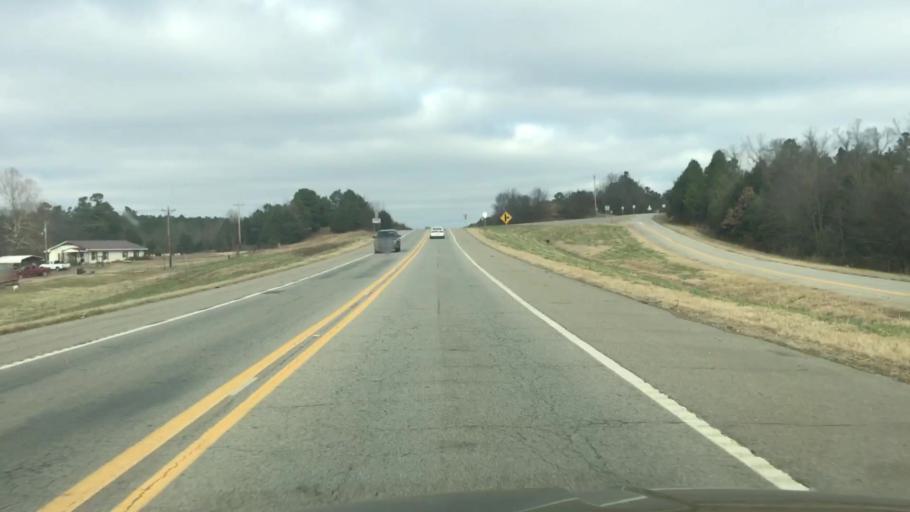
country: US
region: Arkansas
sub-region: Scott County
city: Waldron
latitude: 34.8548
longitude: -94.0660
